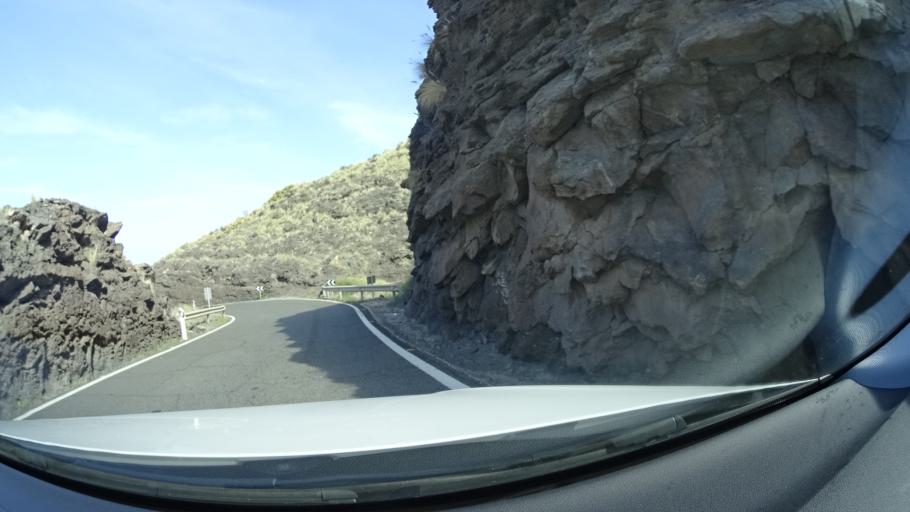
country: ES
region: Canary Islands
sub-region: Provincia de Las Palmas
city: Agaete
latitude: 28.0417
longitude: -15.7350
